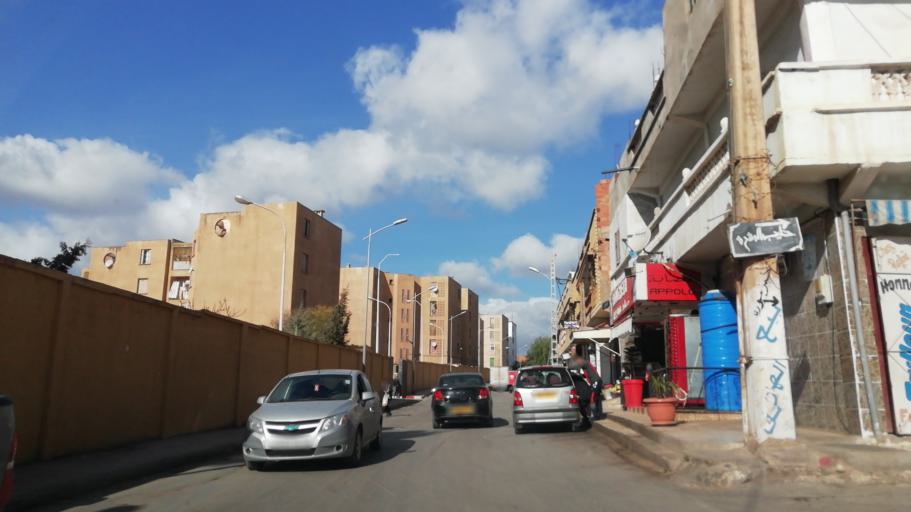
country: DZ
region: Oran
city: Es Senia
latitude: 35.6415
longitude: -0.6696
